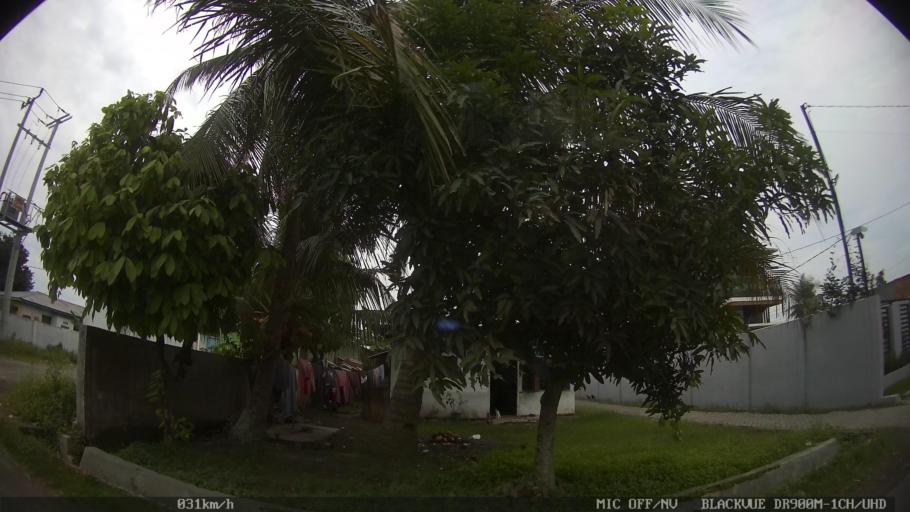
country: ID
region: North Sumatra
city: Sunggal
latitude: 3.6296
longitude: 98.5589
